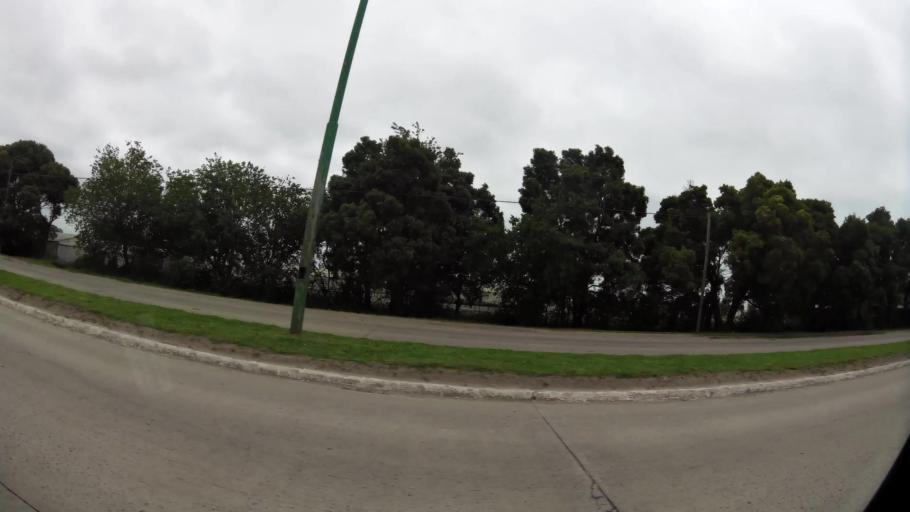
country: AR
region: Buenos Aires
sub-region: Partido de La Plata
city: La Plata
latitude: -35.0259
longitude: -58.0819
